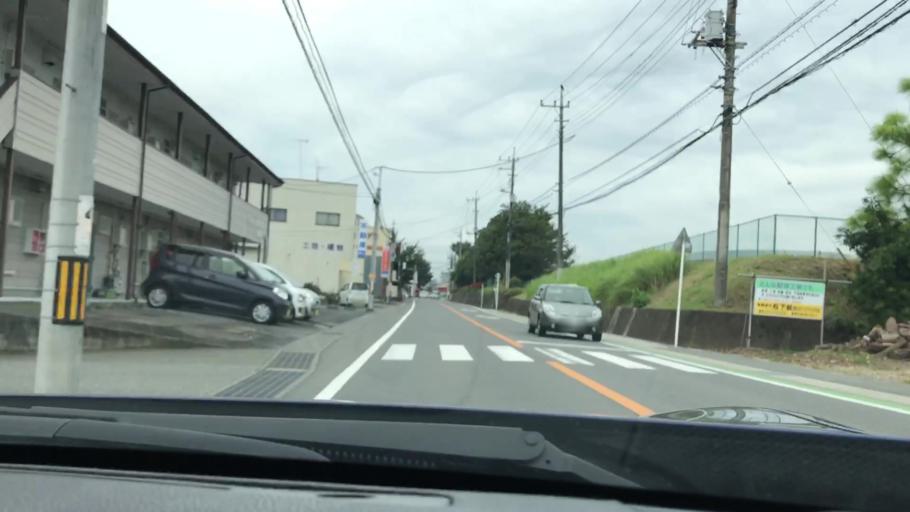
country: JP
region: Gunma
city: Kanekomachi
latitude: 36.3959
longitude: 139.0016
